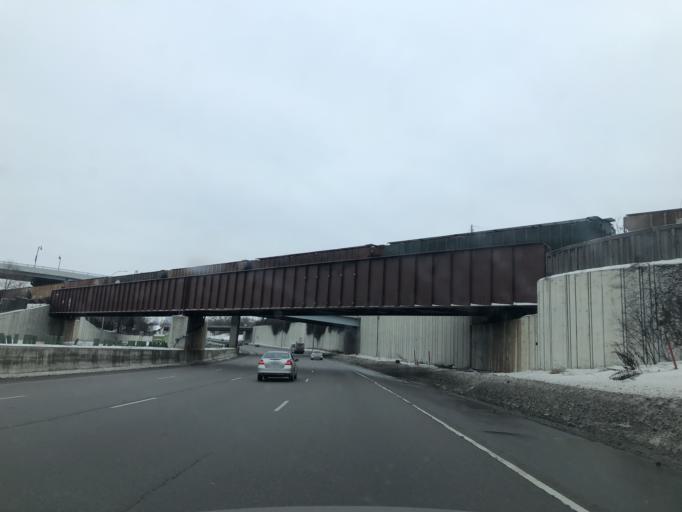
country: US
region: Minnesota
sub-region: Anoka County
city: Columbia Heights
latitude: 45.0328
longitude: -93.2876
